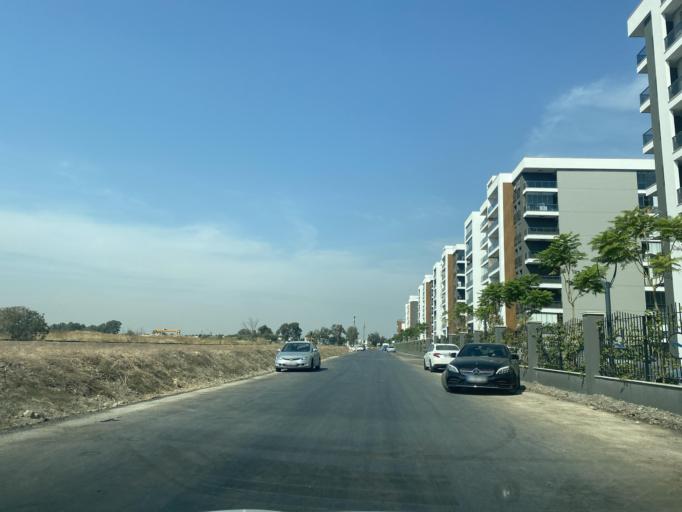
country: TR
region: Izmir
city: Karsiyaka
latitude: 38.4899
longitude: 27.0494
